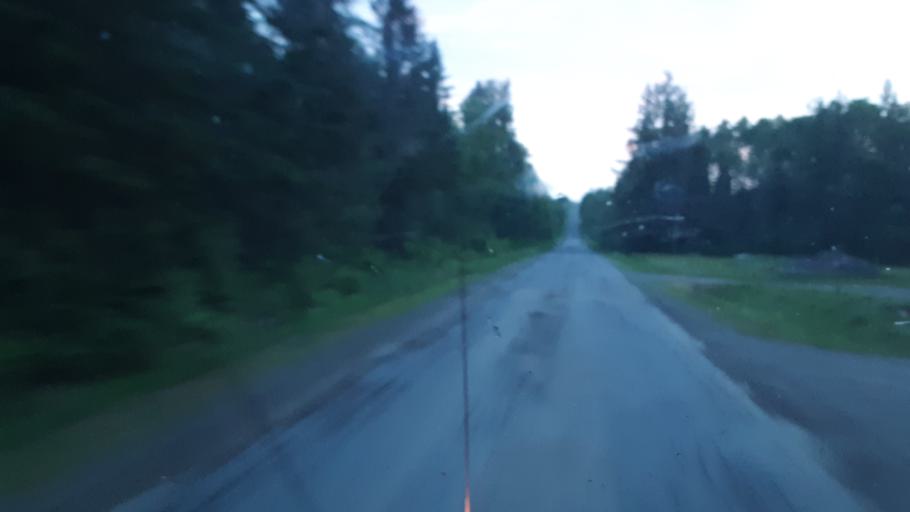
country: US
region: Maine
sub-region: Aroostook County
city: Caribou
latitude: 46.8517
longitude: -68.0919
